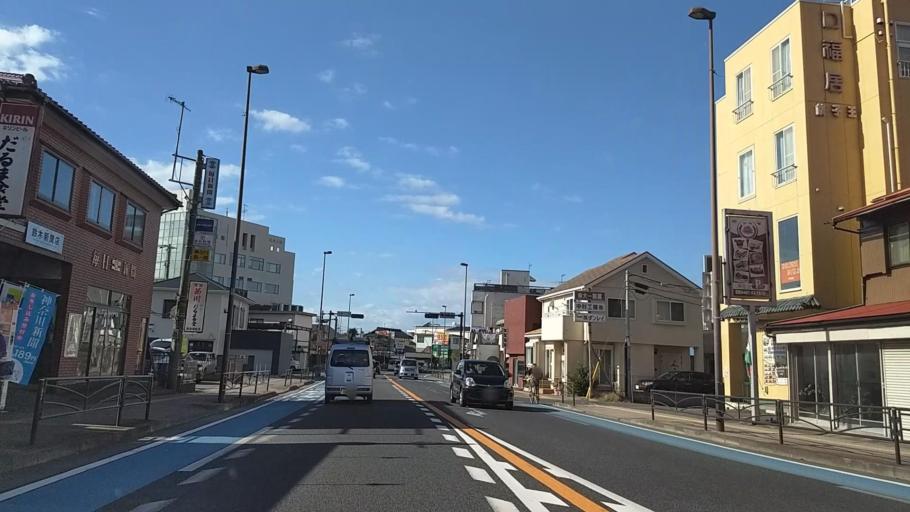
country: JP
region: Kanagawa
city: Chigasaki
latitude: 35.3288
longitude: 139.3938
